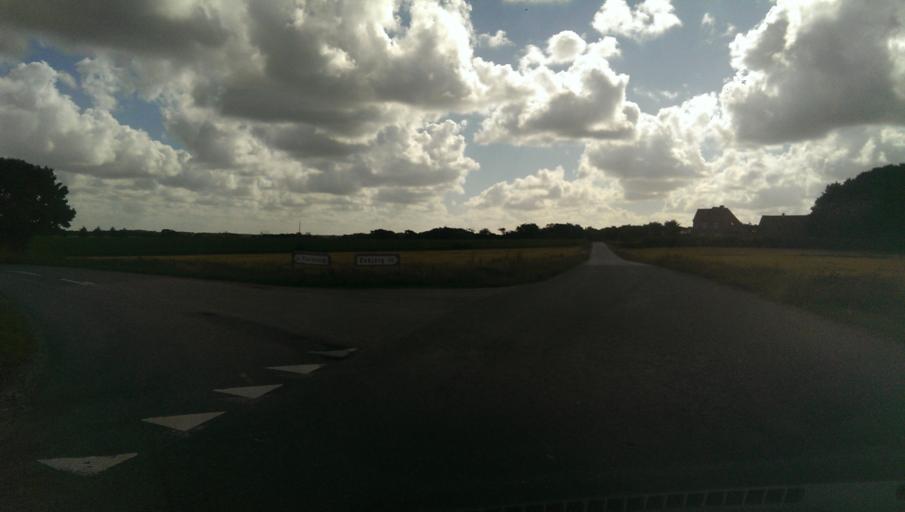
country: DK
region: South Denmark
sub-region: Esbjerg Kommune
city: Tjaereborg
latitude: 55.5136
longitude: 8.5776
